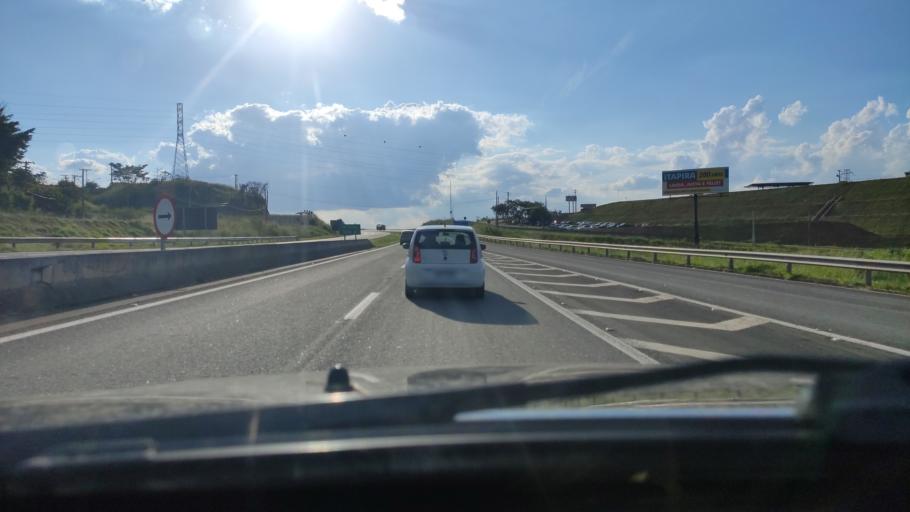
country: BR
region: Sao Paulo
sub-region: Itapira
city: Itapira
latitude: -22.4515
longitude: -46.8440
